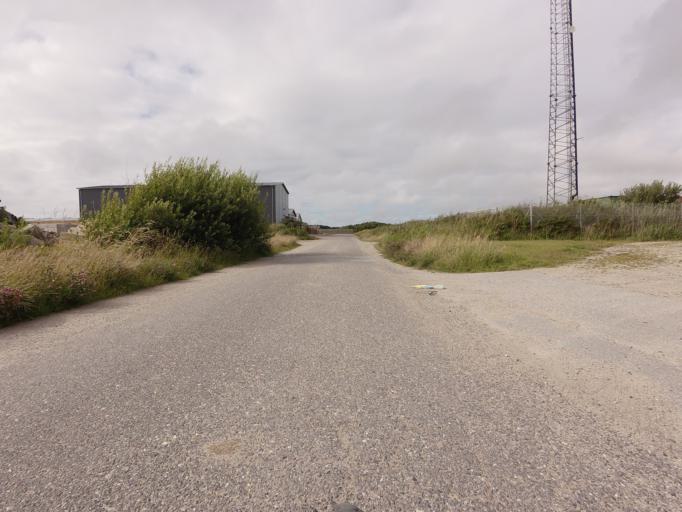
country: DK
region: North Denmark
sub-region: Jammerbugt Kommune
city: Pandrup
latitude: 57.3718
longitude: 9.7312
